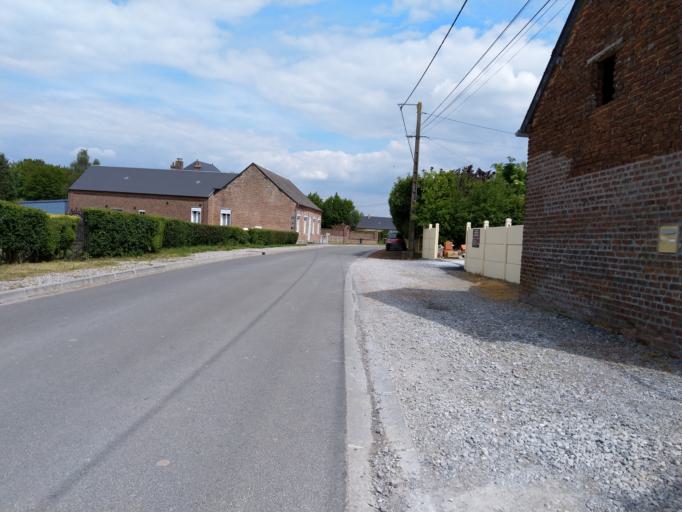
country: FR
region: Picardie
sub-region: Departement de l'Aisne
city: Boue
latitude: 50.0415
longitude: 3.6704
